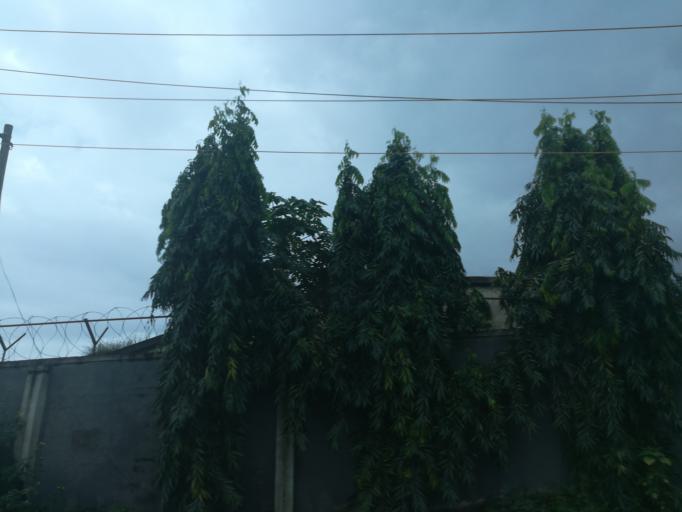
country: NG
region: Lagos
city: Agege
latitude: 6.6148
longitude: 3.3382
